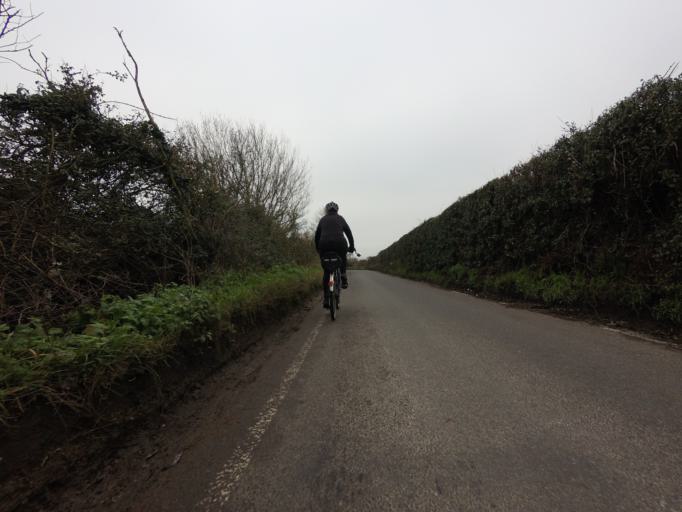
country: GB
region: England
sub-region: Kent
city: Swanley
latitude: 51.3847
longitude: 0.1871
